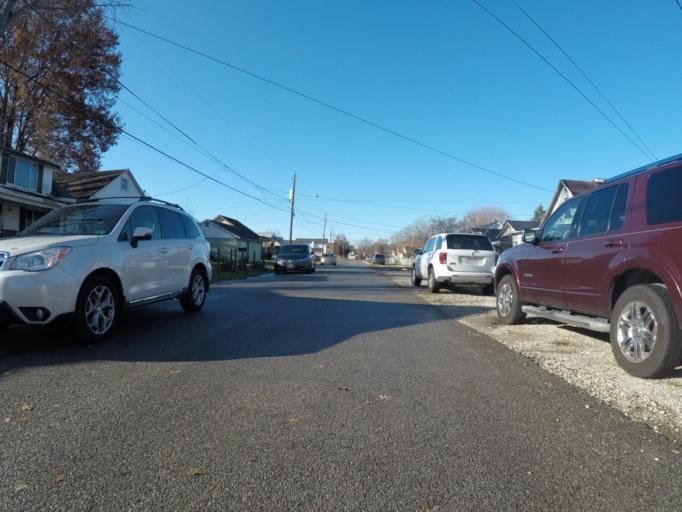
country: US
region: West Virginia
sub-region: Cabell County
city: Huntington
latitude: 38.4119
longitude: -82.4886
